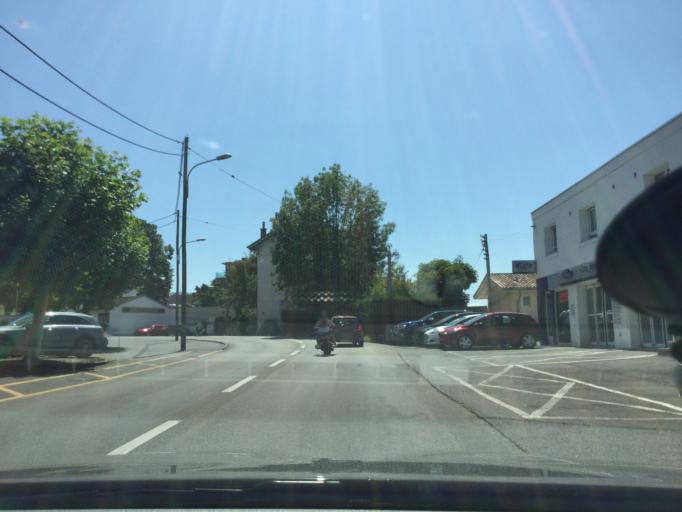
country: CH
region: Geneva
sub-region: Geneva
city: Vandoeuvres
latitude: 46.2408
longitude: 6.1978
